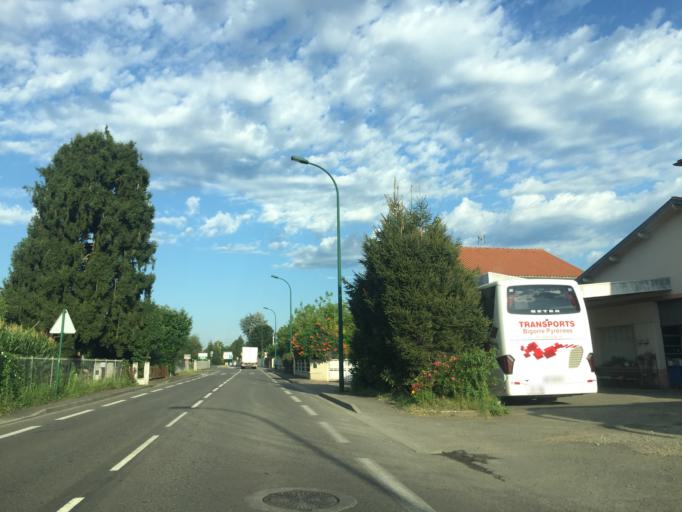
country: FR
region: Midi-Pyrenees
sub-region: Departement des Hautes-Pyrenees
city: Lourdes
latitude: 43.0963
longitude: -0.0237
